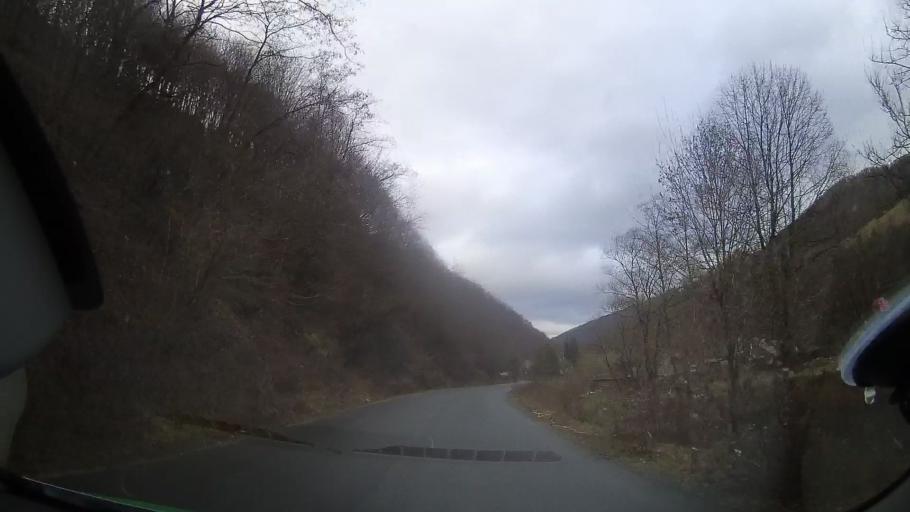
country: RO
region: Cluj
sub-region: Comuna Maguri-Racatau
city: Maguri-Racatau
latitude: 46.6515
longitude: 23.1994
